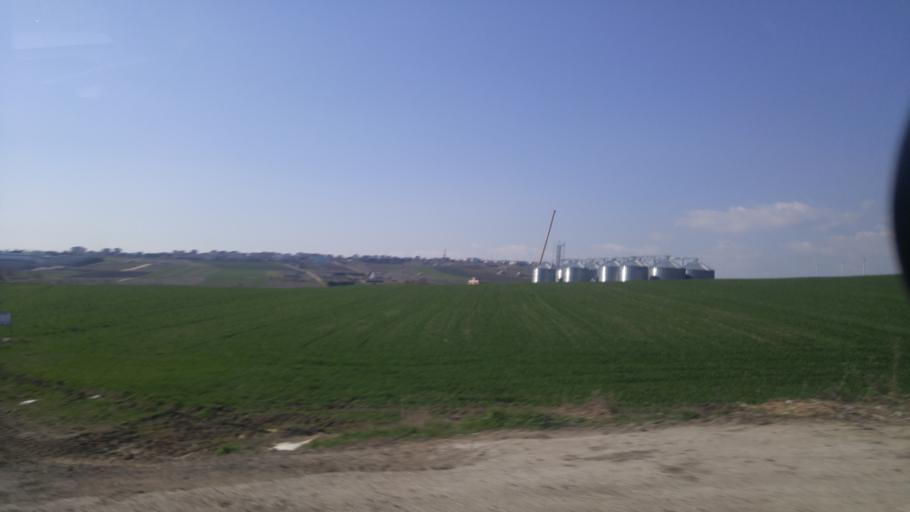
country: TR
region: Istanbul
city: Canta
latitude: 41.0803
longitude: 28.1069
